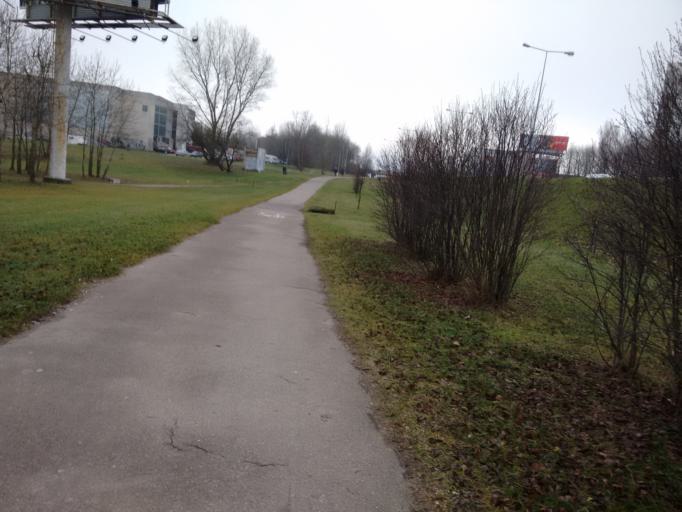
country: LT
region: Vilnius County
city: Seskine
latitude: 54.7196
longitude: 25.2456
